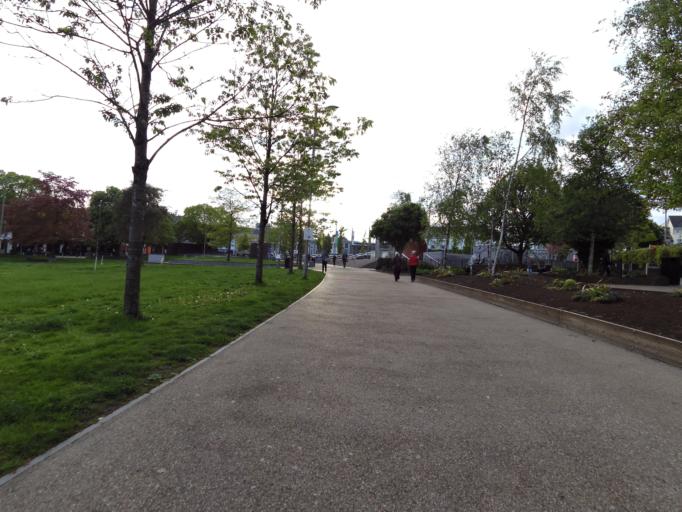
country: IE
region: Connaught
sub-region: County Galway
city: Gaillimh
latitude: 53.2744
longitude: -9.0487
